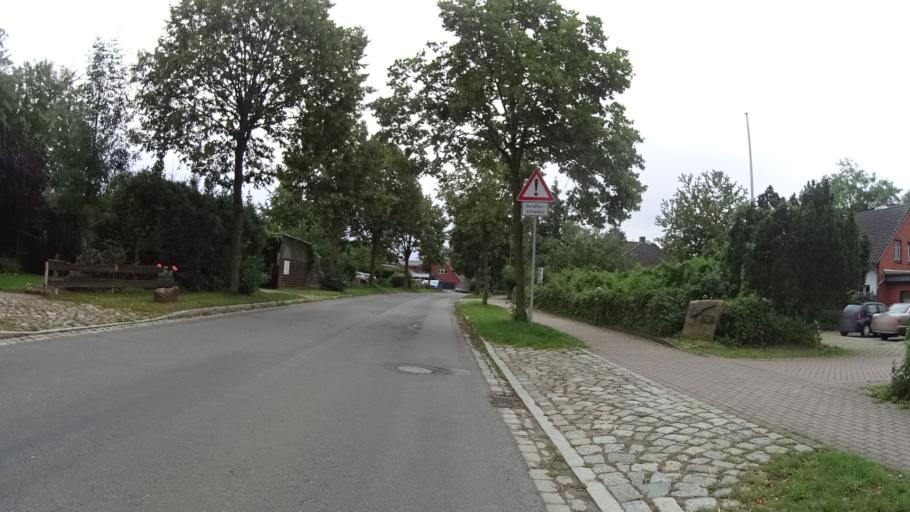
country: DE
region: Schleswig-Holstein
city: Duvensee
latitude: 53.6979
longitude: 10.5679
